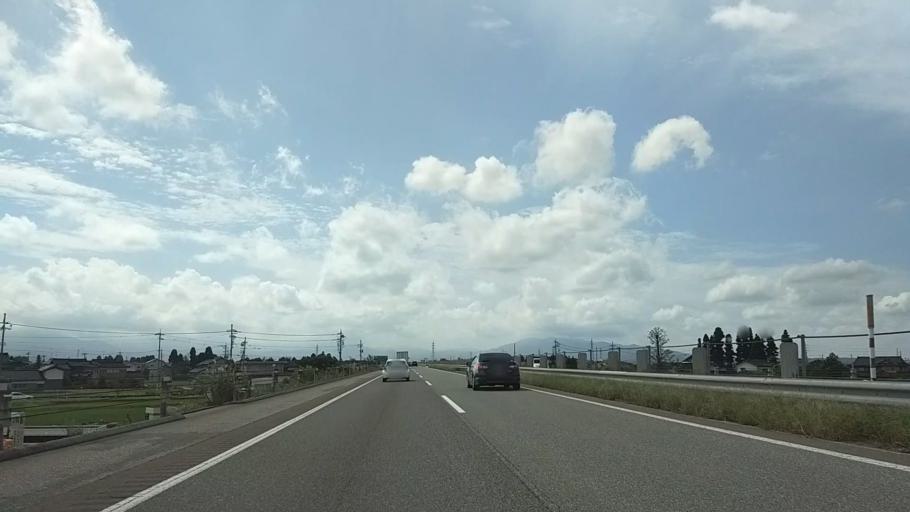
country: JP
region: Toyama
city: Nanto-shi
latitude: 36.6387
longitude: 136.9726
